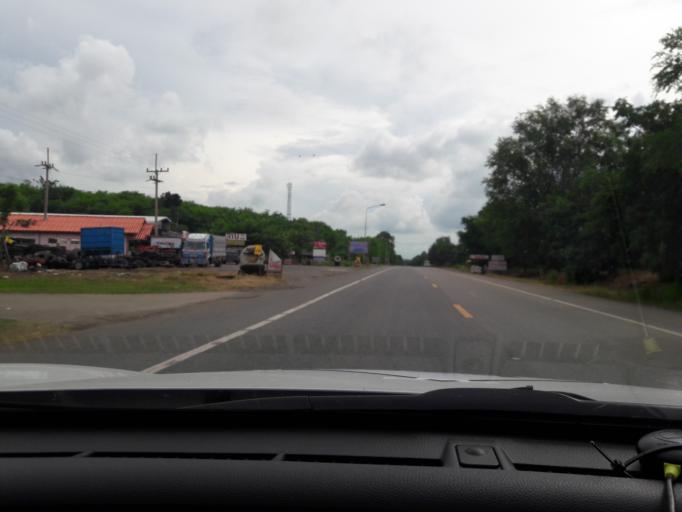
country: TH
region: Nakhon Sawan
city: Tak Fa
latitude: 15.3936
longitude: 100.5095
